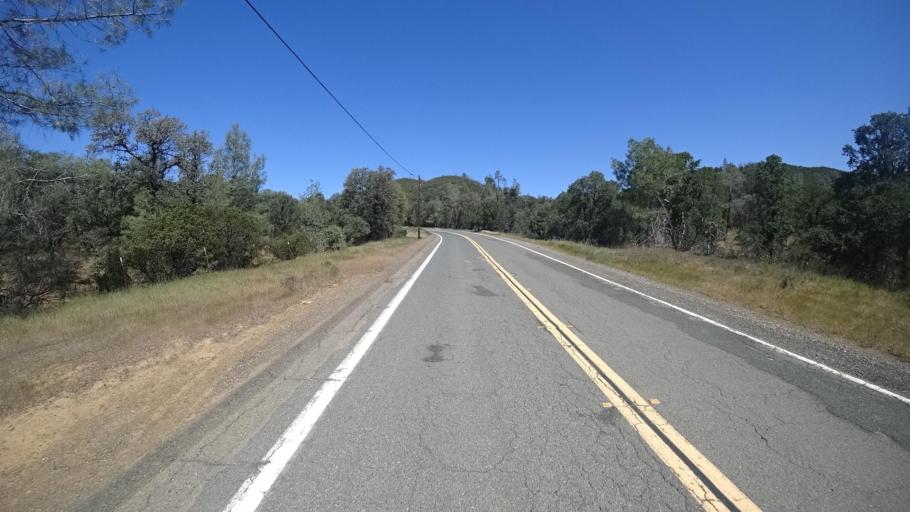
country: US
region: California
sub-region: Lake County
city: Hidden Valley Lake
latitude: 38.8781
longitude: -122.4334
